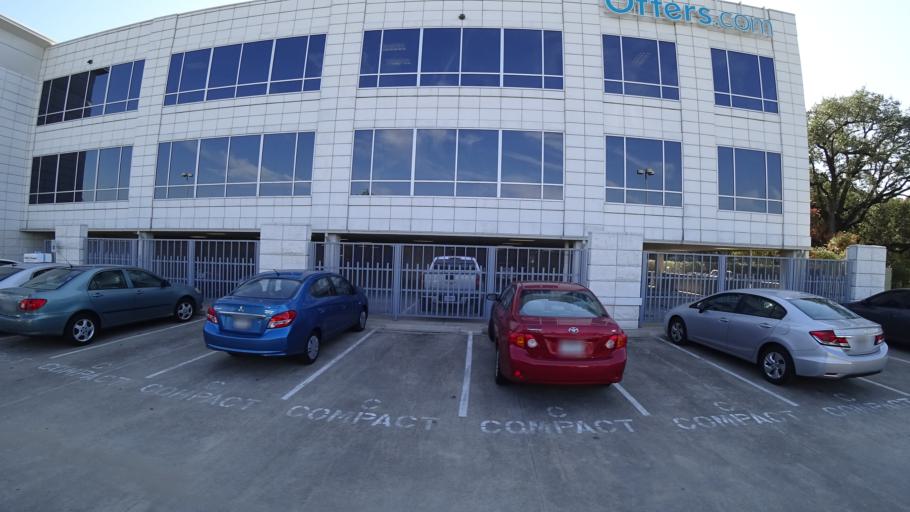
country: US
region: Texas
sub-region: Williamson County
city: Jollyville
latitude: 30.3767
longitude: -97.7785
